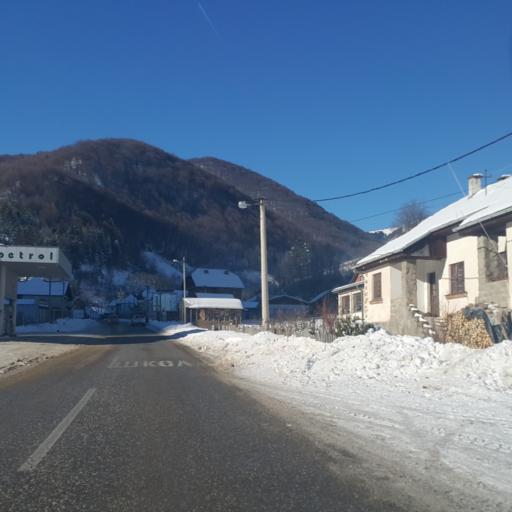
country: XK
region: Mitrovica
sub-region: Komuna e Leposaviqit
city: Leposaviq
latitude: 43.3019
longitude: 20.8895
